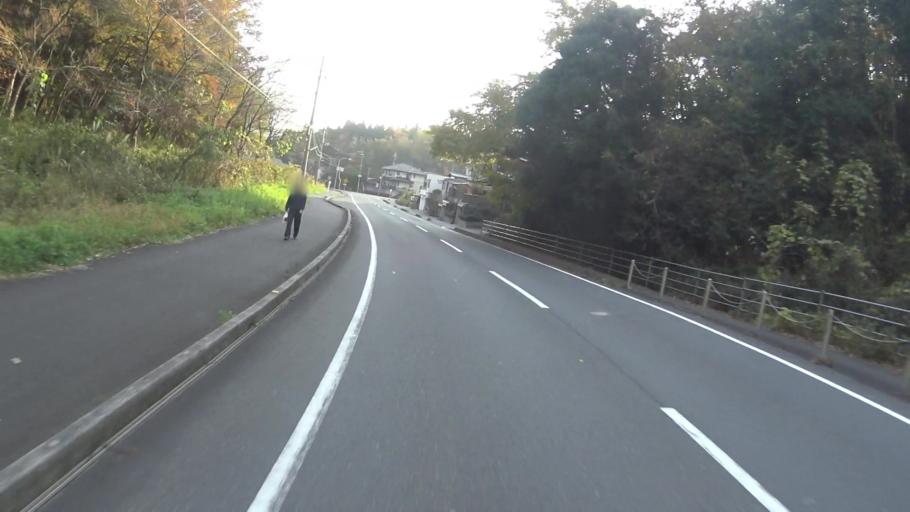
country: JP
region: Kyoto
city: Maizuru
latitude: 35.4933
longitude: 135.4372
